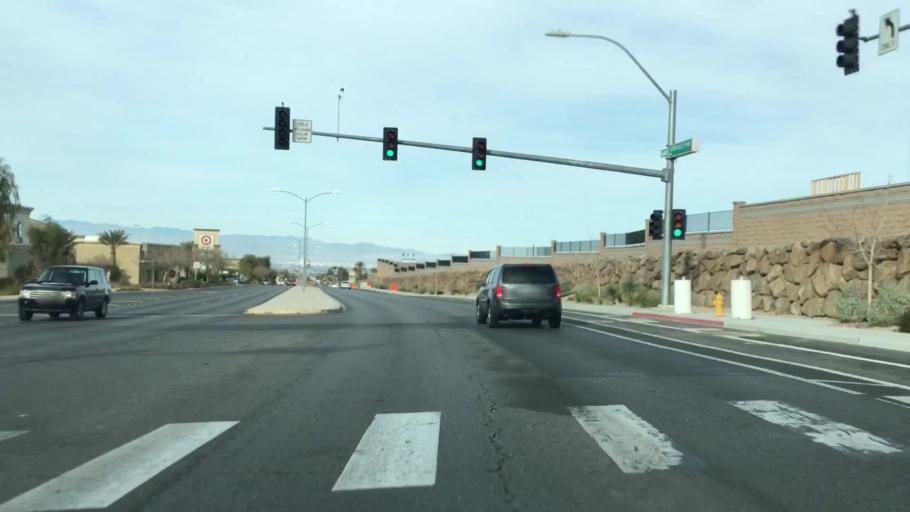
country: US
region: Nevada
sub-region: Clark County
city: Whitney
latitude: 36.0003
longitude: -115.0832
